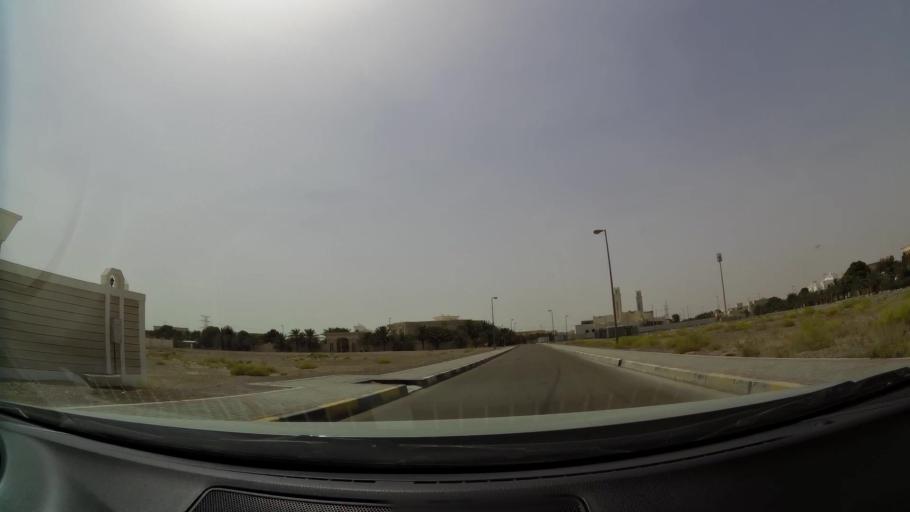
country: AE
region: Abu Dhabi
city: Al Ain
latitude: 24.1609
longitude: 55.6611
